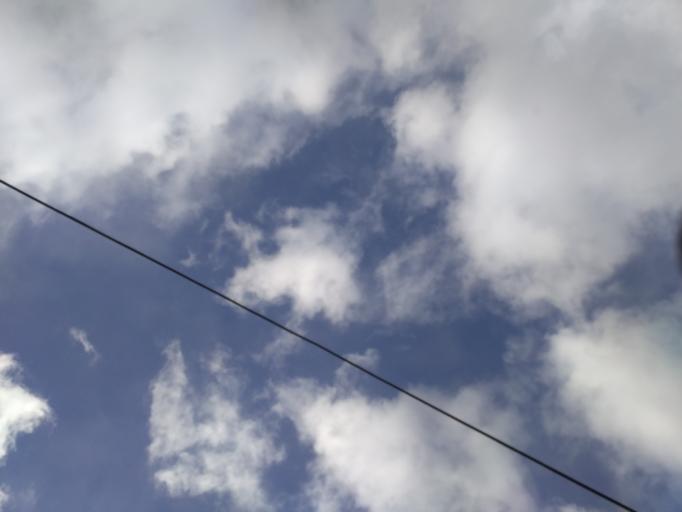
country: SK
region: Kosicky
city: Secovce
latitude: 48.6932
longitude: 21.6526
